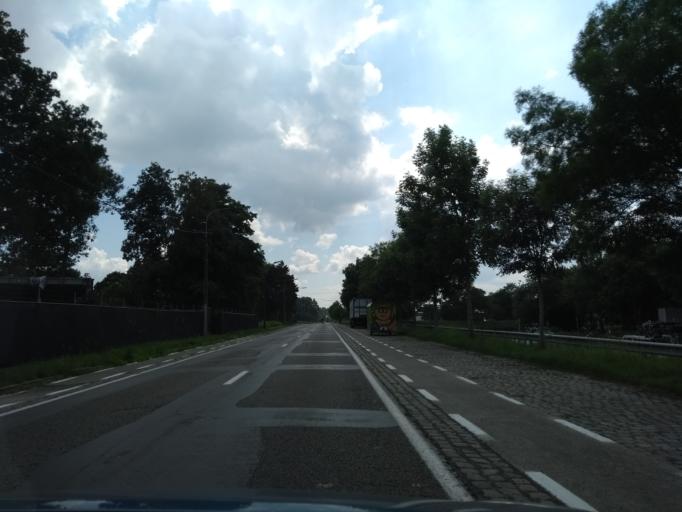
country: BE
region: Flanders
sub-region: Provincie Oost-Vlaanderen
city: Eeklo
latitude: 51.1769
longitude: 3.5483
